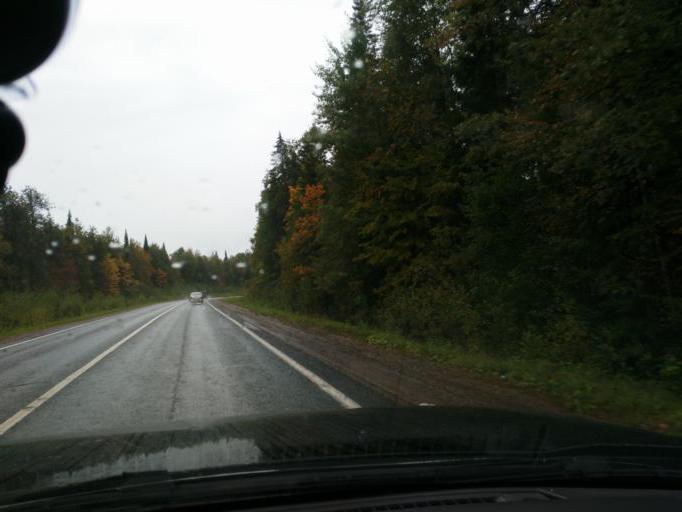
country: RU
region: Perm
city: Yugo-Kamskiy
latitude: 57.5966
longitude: 55.6569
